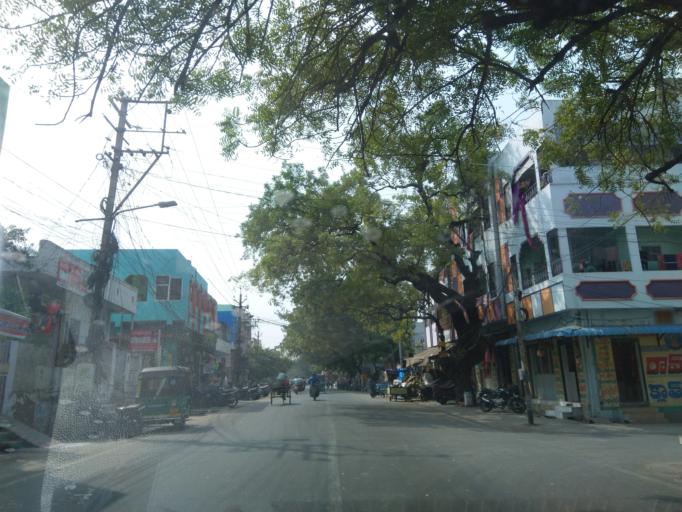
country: IN
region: Andhra Pradesh
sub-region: Krishna
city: Vijayawada
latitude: 16.5296
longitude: 80.6053
